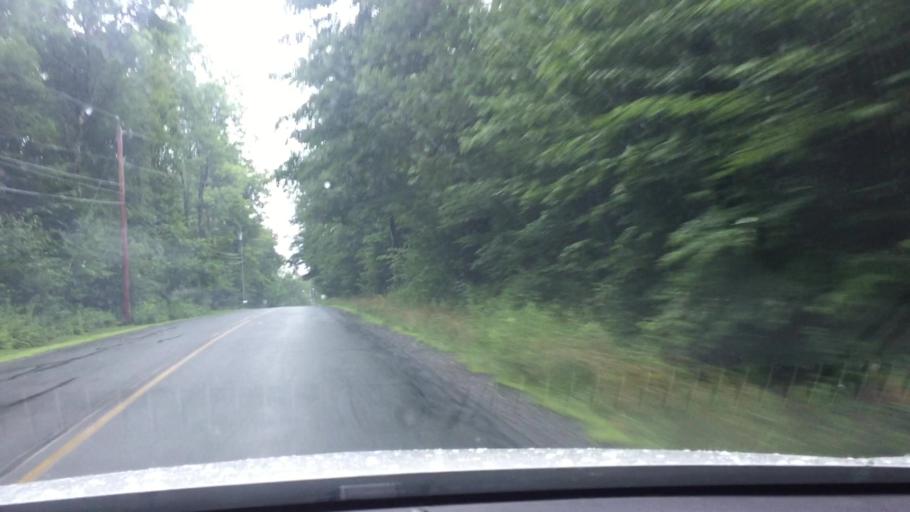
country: US
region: Massachusetts
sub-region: Berkshire County
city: Becket
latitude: 42.2900
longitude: -73.0564
